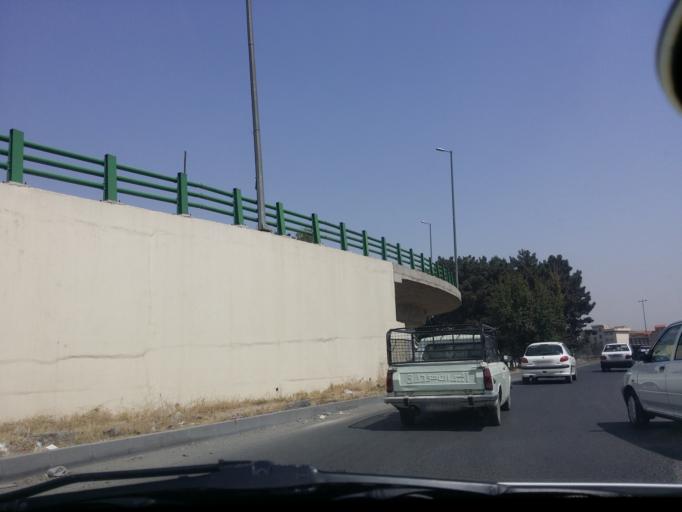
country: IR
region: Alborz
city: Karaj
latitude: 35.8495
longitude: 50.9079
